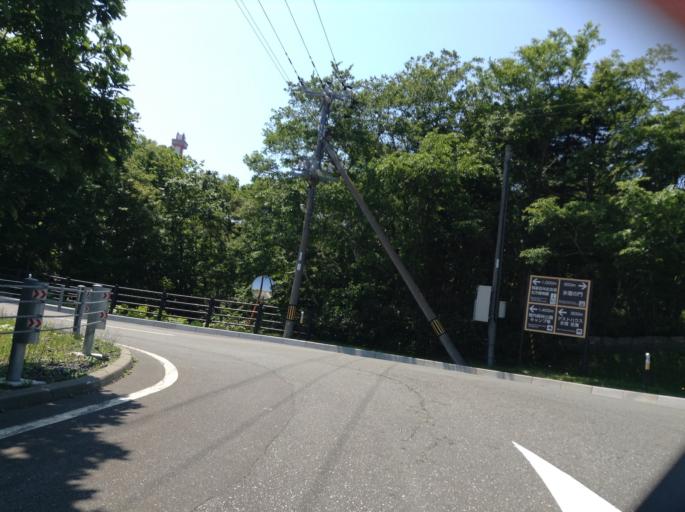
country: JP
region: Hokkaido
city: Wakkanai
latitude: 45.4199
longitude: 141.6690
